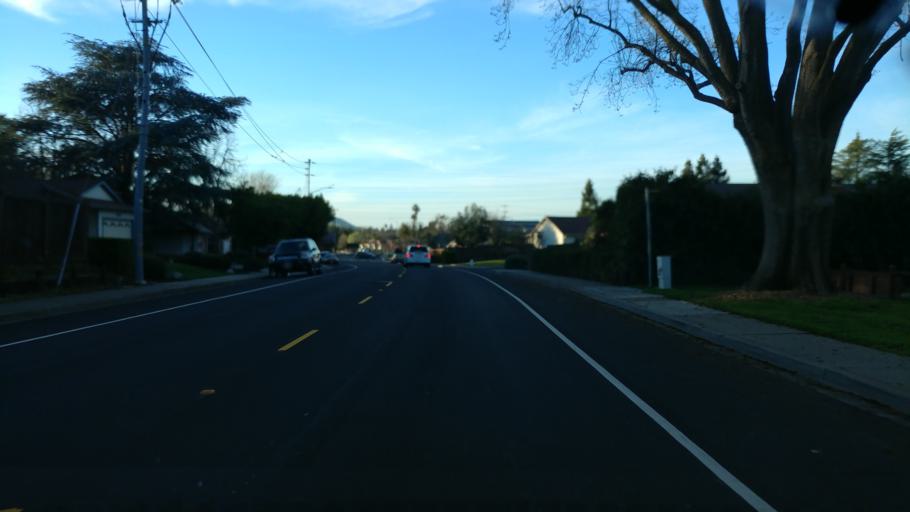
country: US
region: California
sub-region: Alameda County
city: Dublin
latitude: 37.7367
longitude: -121.9470
